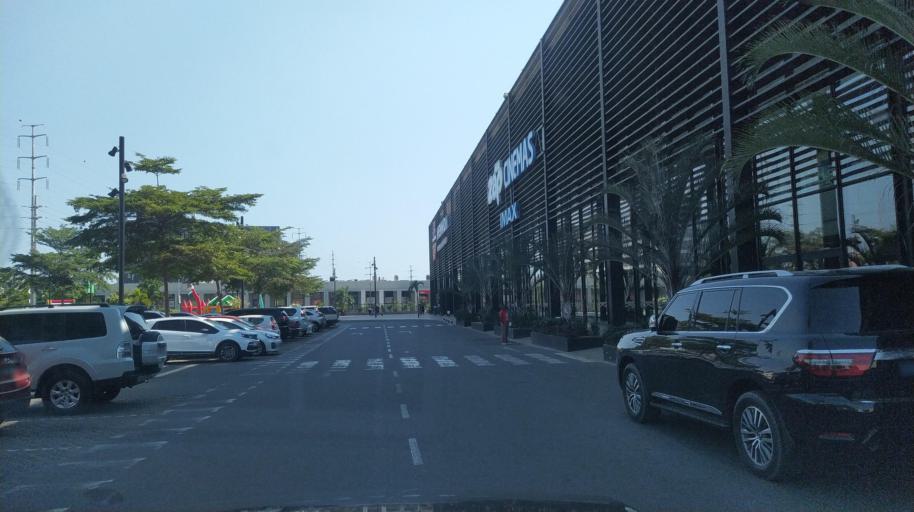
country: AO
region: Luanda
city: Luanda
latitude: -8.9032
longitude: 13.1900
